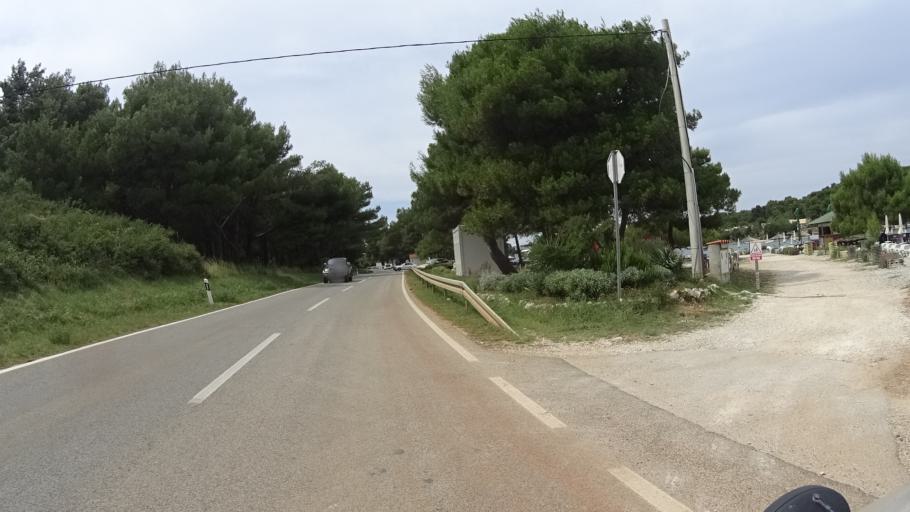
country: HR
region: Istarska
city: Medulin
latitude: 44.8155
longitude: 13.8998
